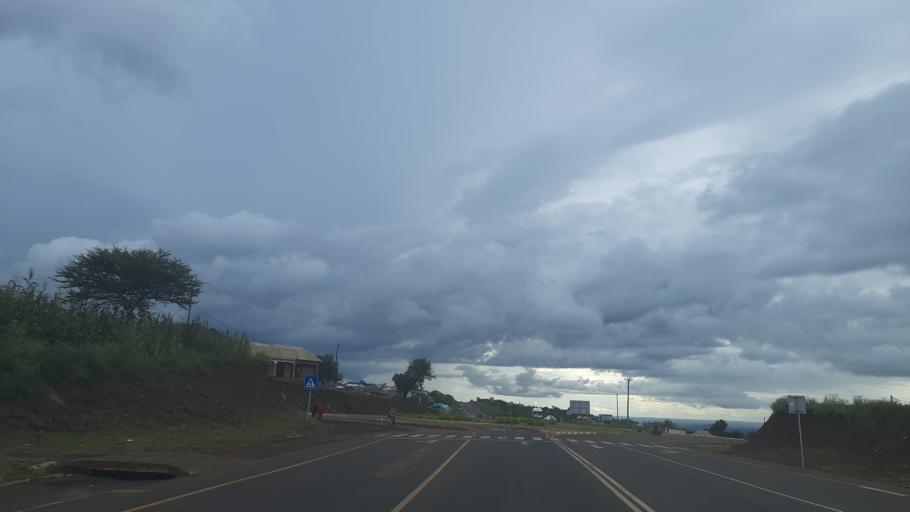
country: TZ
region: Arusha
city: Arusha
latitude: -3.4354
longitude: 36.6435
